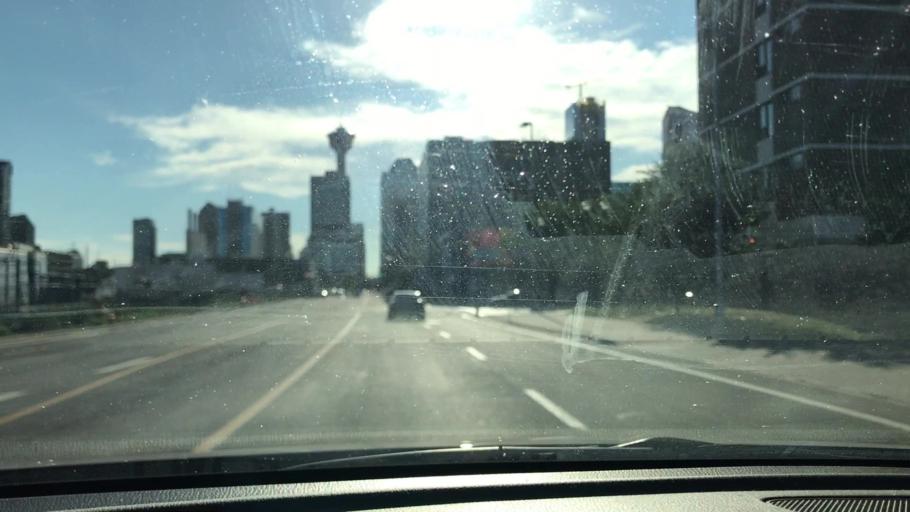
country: CA
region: Alberta
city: Calgary
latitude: 51.0443
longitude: -114.0499
